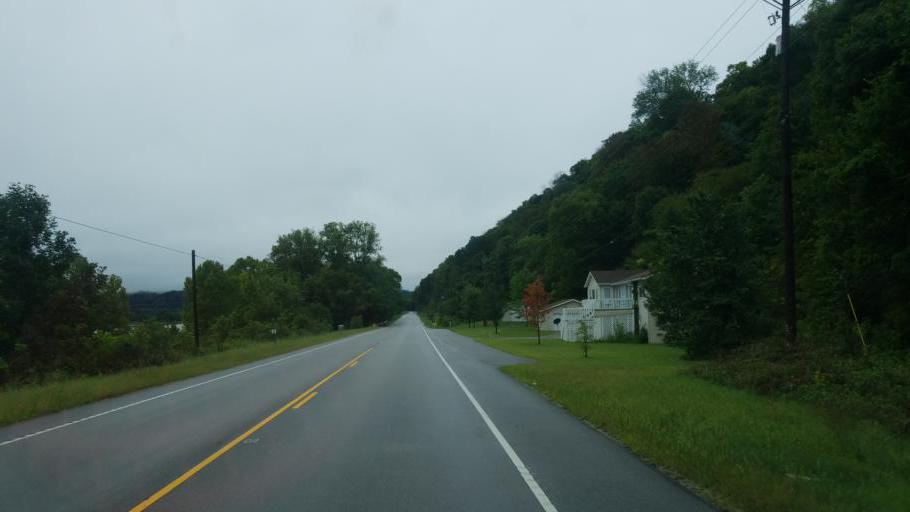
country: US
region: Ohio
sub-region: Adams County
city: Manchester
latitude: 38.6650
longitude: -83.6387
